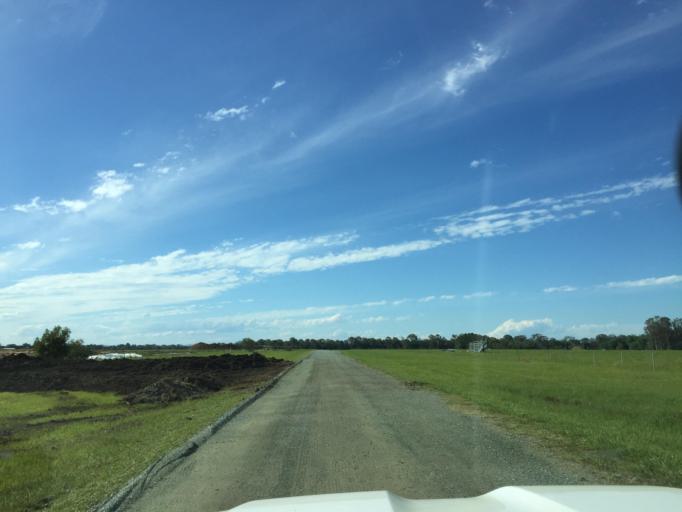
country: AU
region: Queensland
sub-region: Moreton Bay
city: Morayfield
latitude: -27.1146
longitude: 152.9942
